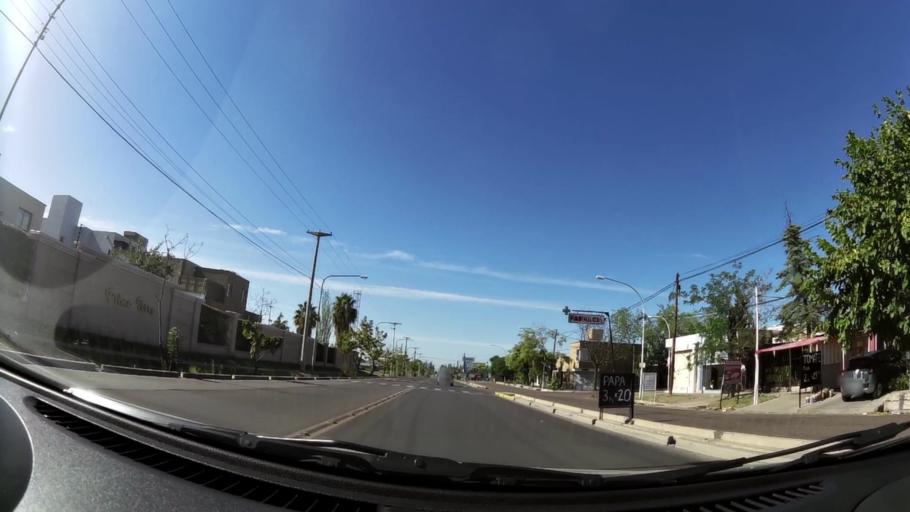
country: AR
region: Mendoza
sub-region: Departamento de Godoy Cruz
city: Godoy Cruz
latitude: -32.9357
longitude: -68.8006
